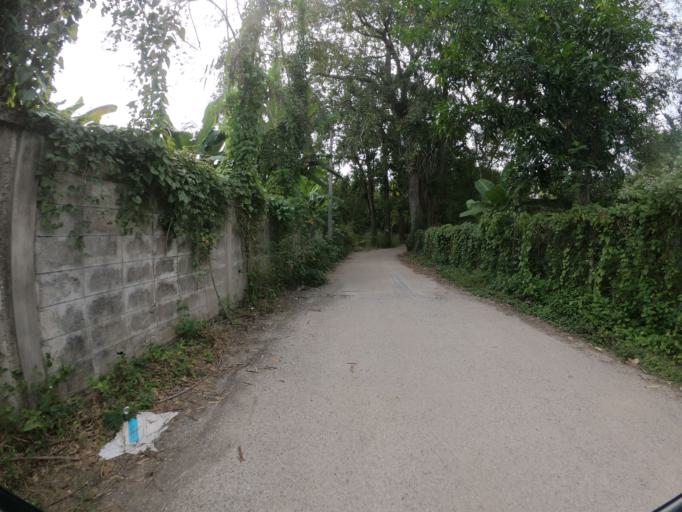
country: TH
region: Chiang Mai
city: Chiang Mai
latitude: 18.7519
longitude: 98.9375
